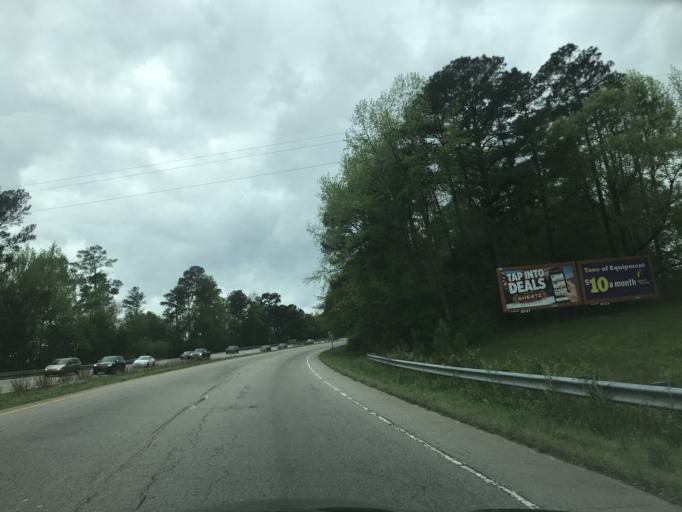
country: US
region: North Carolina
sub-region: Wake County
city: Knightdale
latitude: 35.7923
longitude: -78.5423
